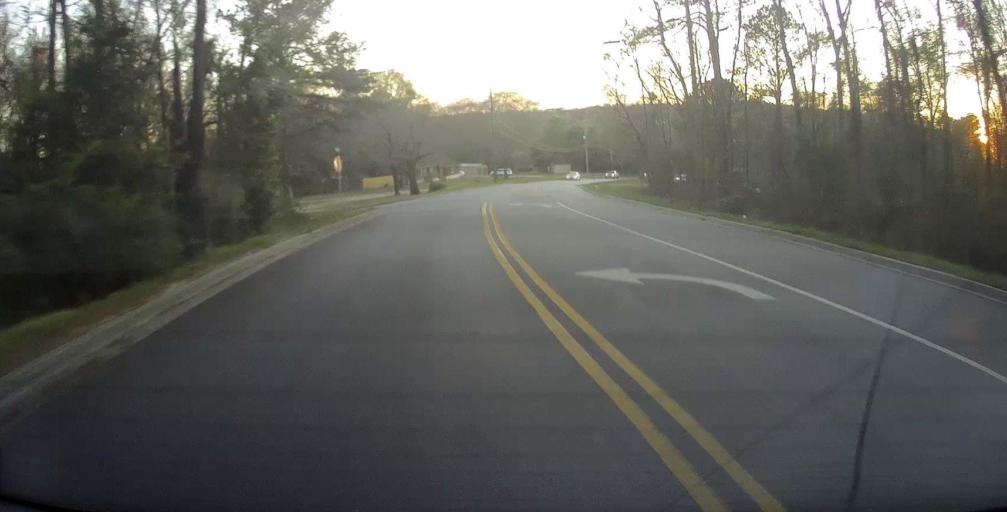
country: US
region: Alabama
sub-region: Russell County
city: Phenix City
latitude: 32.4863
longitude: -85.0213
